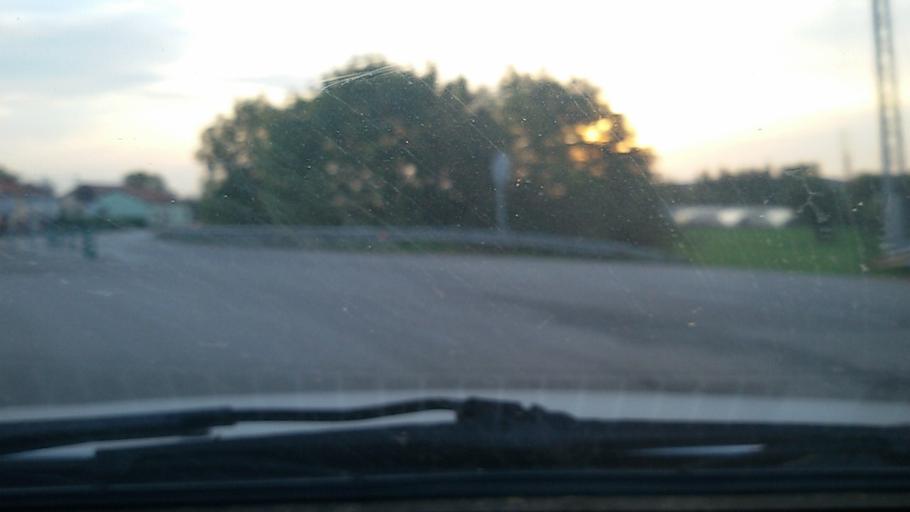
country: ES
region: Asturias
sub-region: Province of Asturias
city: Norena
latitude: 43.3865
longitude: -5.7252
